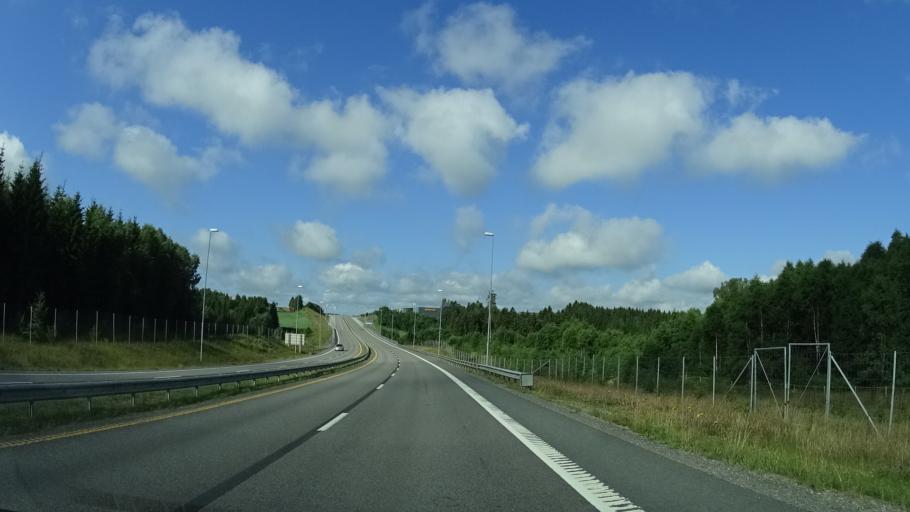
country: NO
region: Ostfold
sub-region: Askim
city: Askim
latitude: 59.5775
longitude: 11.2305
